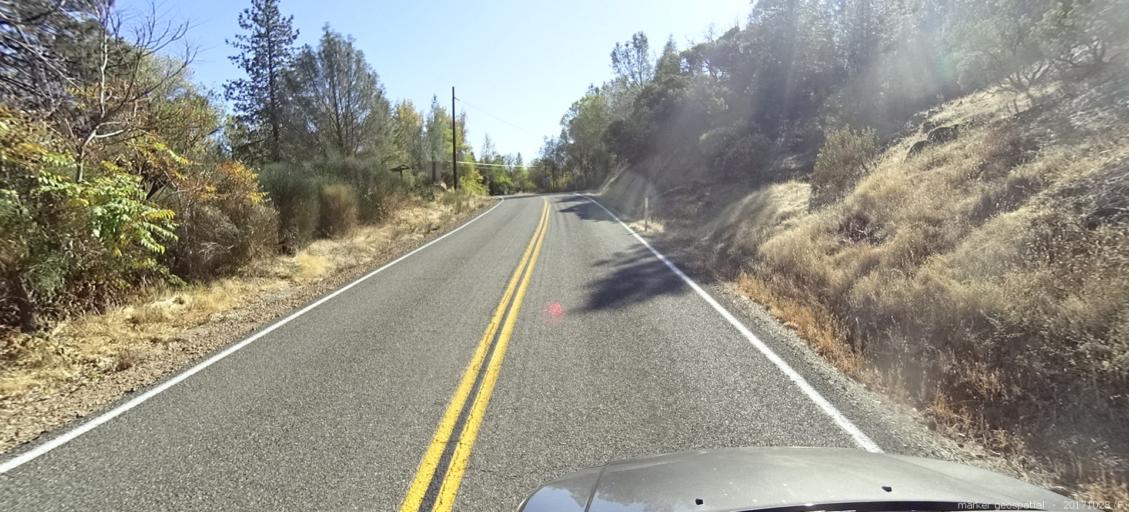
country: US
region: California
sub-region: Shasta County
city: Shasta
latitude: 40.6251
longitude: -122.4664
